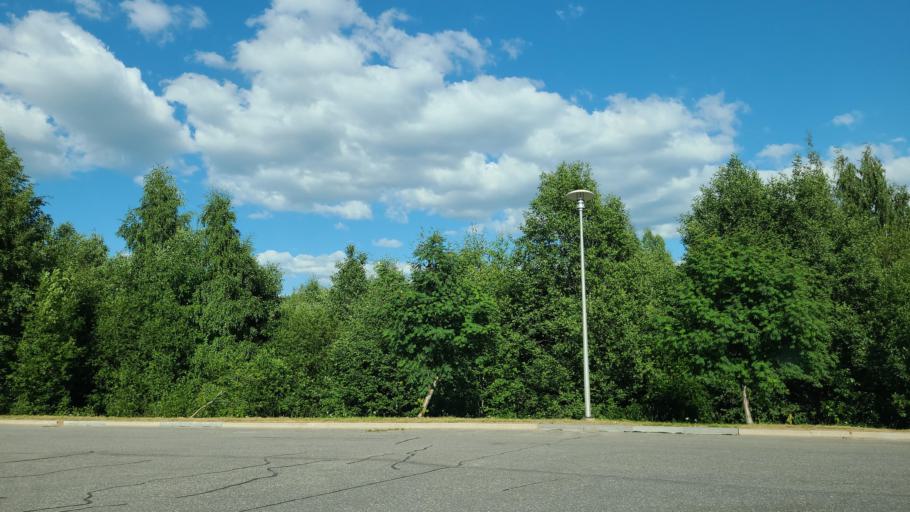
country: FI
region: Central Finland
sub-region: Jyvaeskylae
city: Jyvaeskylae
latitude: 62.2486
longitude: 25.7767
